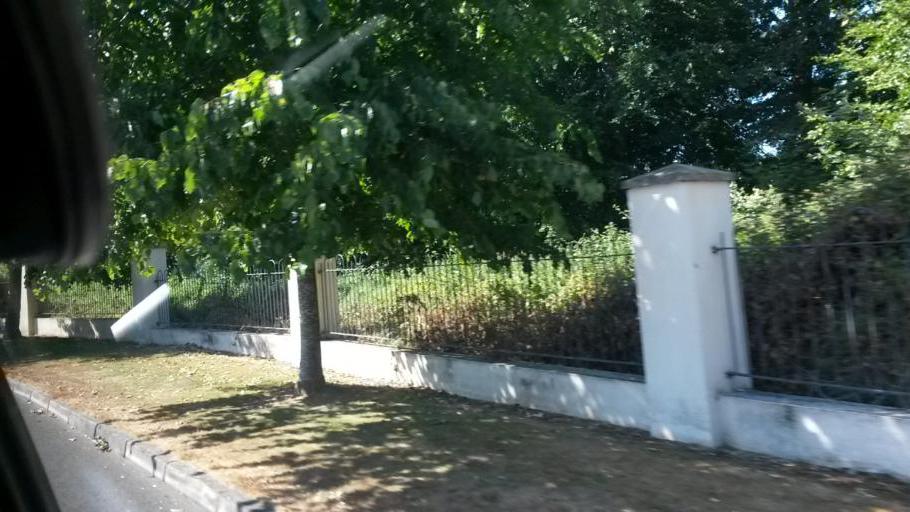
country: IE
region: Leinster
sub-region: Fingal County
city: Swords
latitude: 53.4568
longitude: -6.2619
